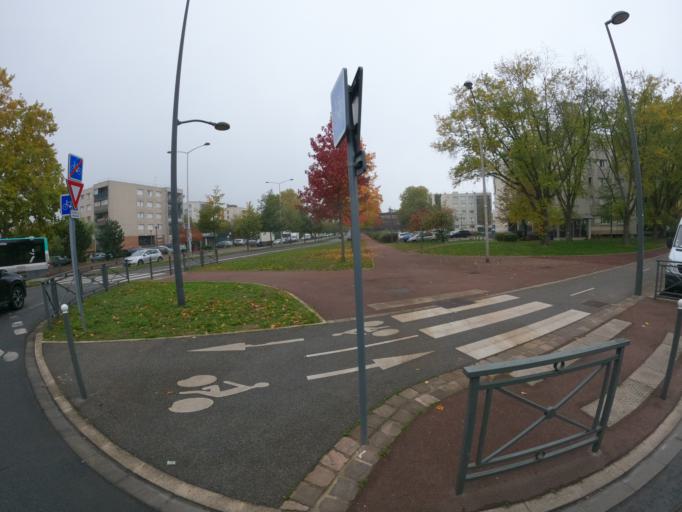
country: FR
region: Ile-de-France
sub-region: Departement du Val-de-Marne
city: Chennevieres-sur-Marne
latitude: 48.8032
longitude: 2.5508
